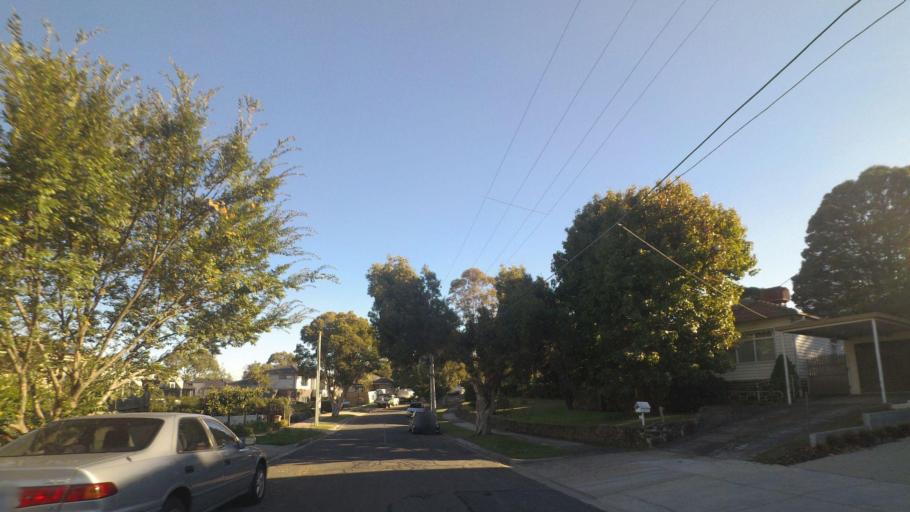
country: AU
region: Victoria
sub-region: Manningham
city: Donvale
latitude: -37.7925
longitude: 145.1649
